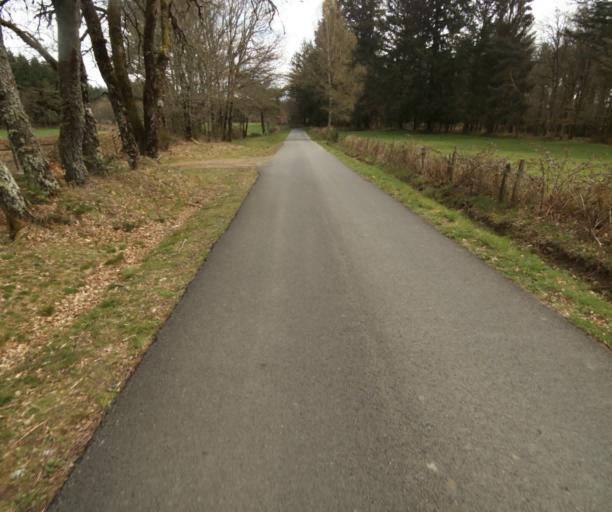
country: FR
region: Limousin
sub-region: Departement de la Correze
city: Correze
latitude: 45.3417
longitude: 1.9598
